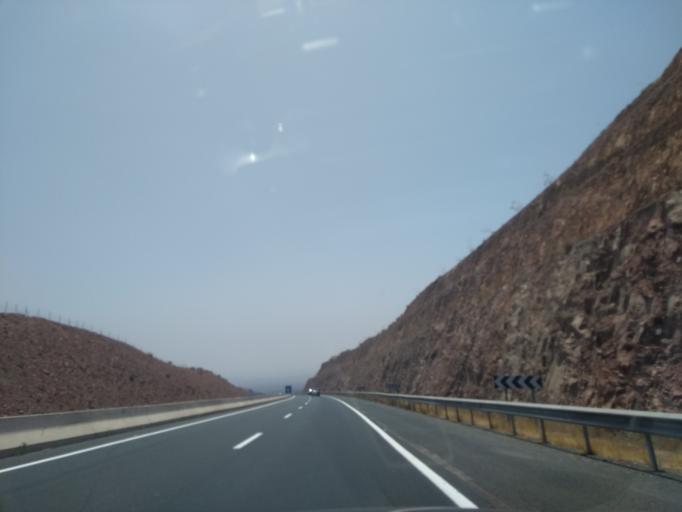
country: MA
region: Souss-Massa-Draa
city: Oulad Teima
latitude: 30.5578
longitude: -9.3363
